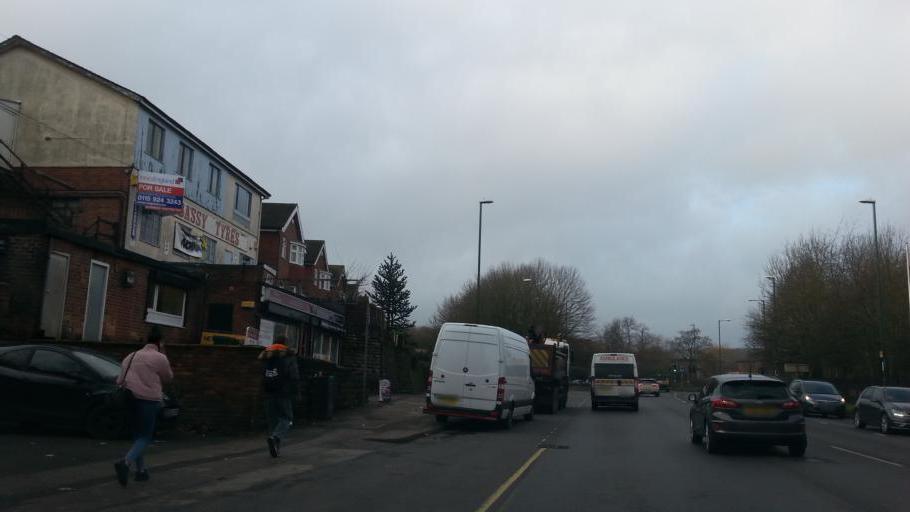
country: GB
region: England
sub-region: Nottinghamshire
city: Hucknall
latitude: 52.9855
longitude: -1.2012
